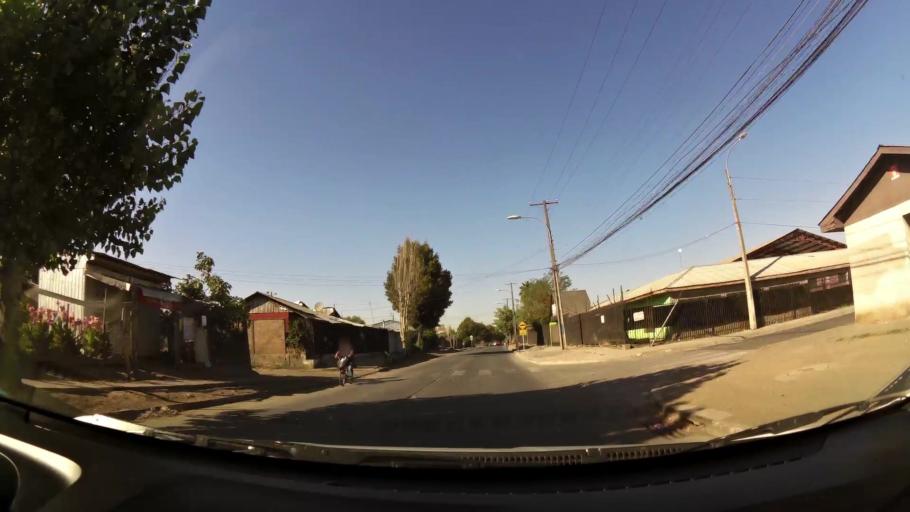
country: CL
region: Maule
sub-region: Provincia de Curico
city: Curico
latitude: -34.9912
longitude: -71.2539
